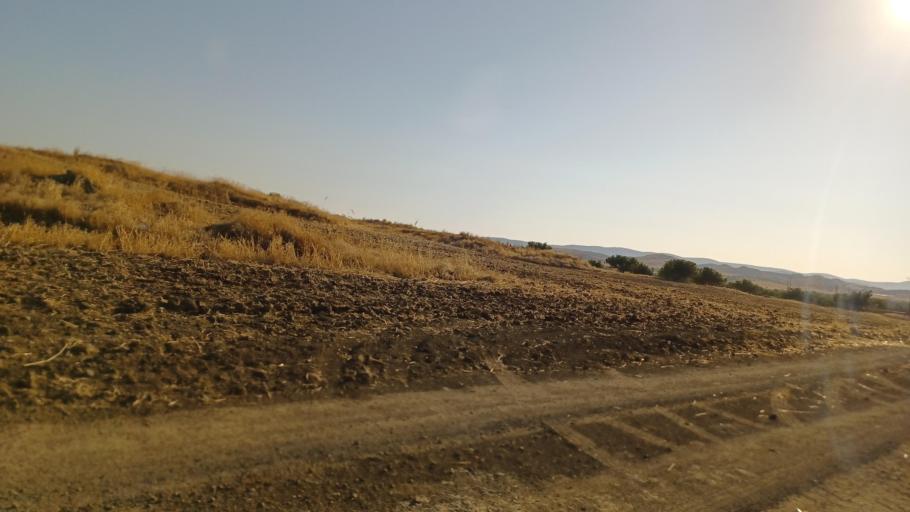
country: CY
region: Larnaka
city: Troulloi
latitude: 35.0152
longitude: 33.5887
